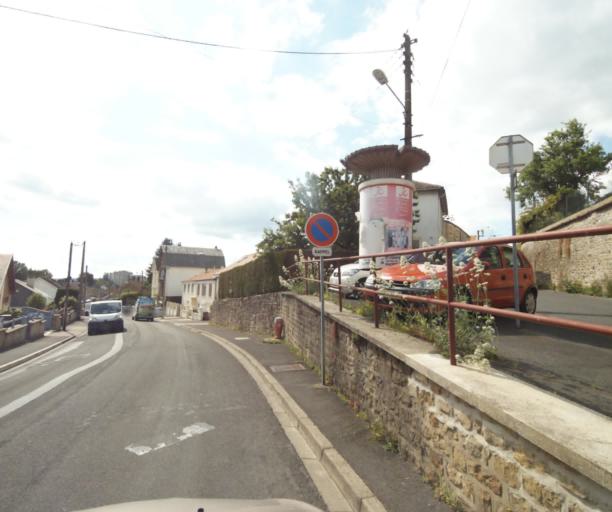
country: FR
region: Champagne-Ardenne
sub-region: Departement des Ardennes
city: Montcy-Notre-Dame
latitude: 49.7591
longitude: 4.7352
